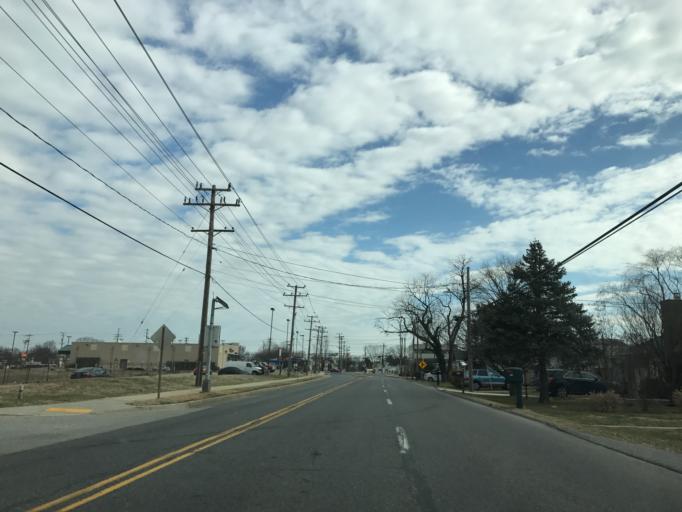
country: US
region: Maryland
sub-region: Anne Arundel County
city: Brooklyn Park
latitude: 39.2156
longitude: -76.6171
